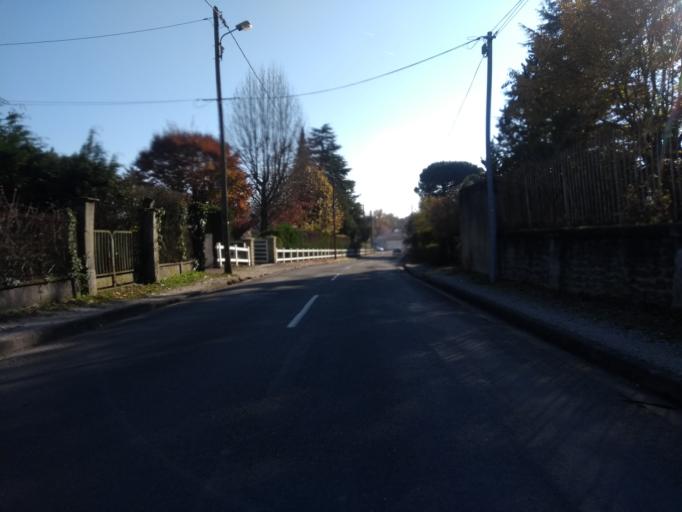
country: FR
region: Aquitaine
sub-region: Departement de la Gironde
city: Leognan
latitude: 44.7342
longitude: -0.6004
